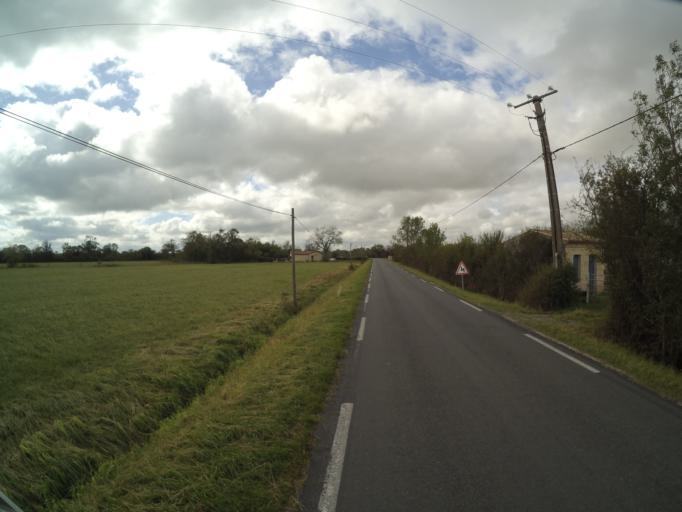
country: FR
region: Aquitaine
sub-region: Departement de la Gironde
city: Ludon-Medoc
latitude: 44.9962
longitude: -0.5921
